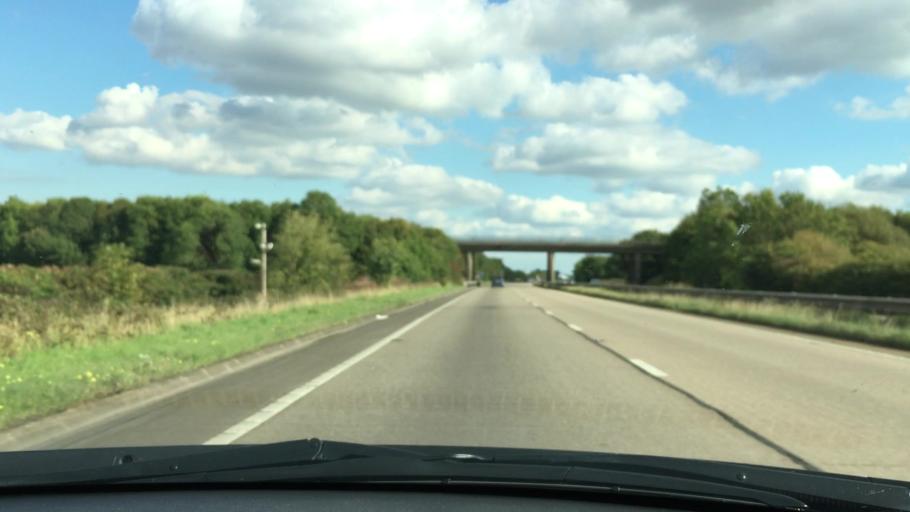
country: GB
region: England
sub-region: North East Lincolnshire
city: Healing
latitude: 53.5945
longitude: -0.1757
